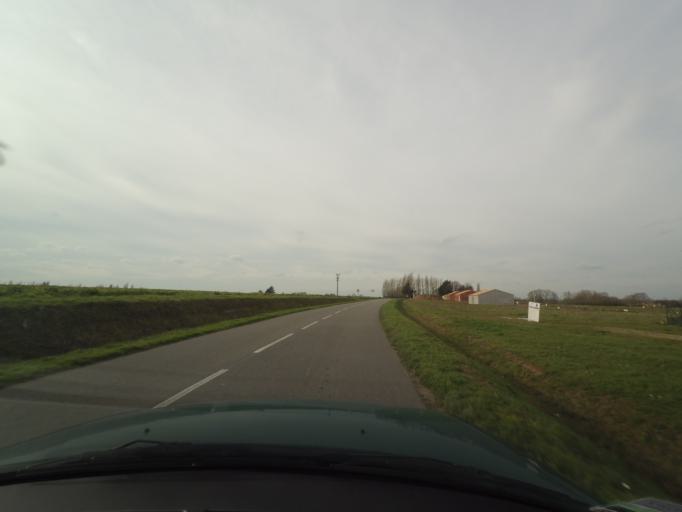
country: FR
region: Pays de la Loire
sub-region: Departement de la Loire-Atlantique
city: Saint-Lumine-de-Coutais
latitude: 47.0481
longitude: -1.7285
